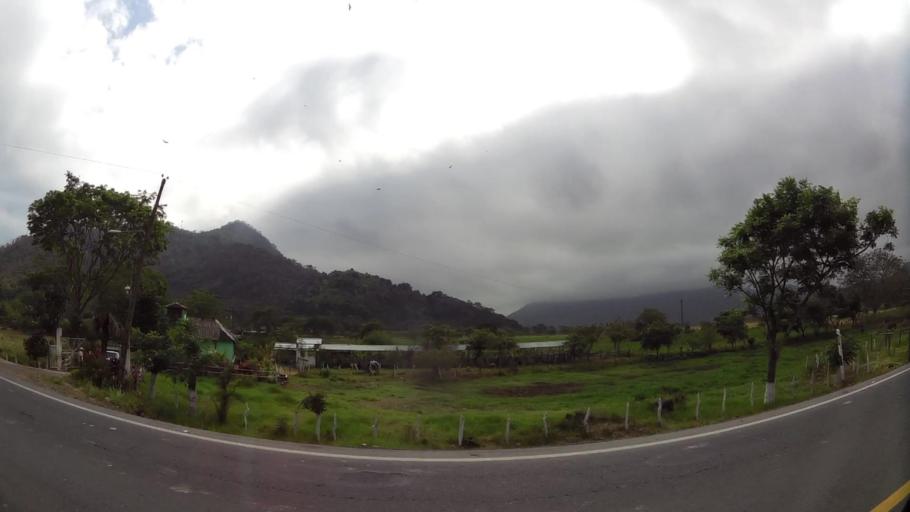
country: EC
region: Guayas
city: Naranjal
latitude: -2.4152
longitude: -79.6242
